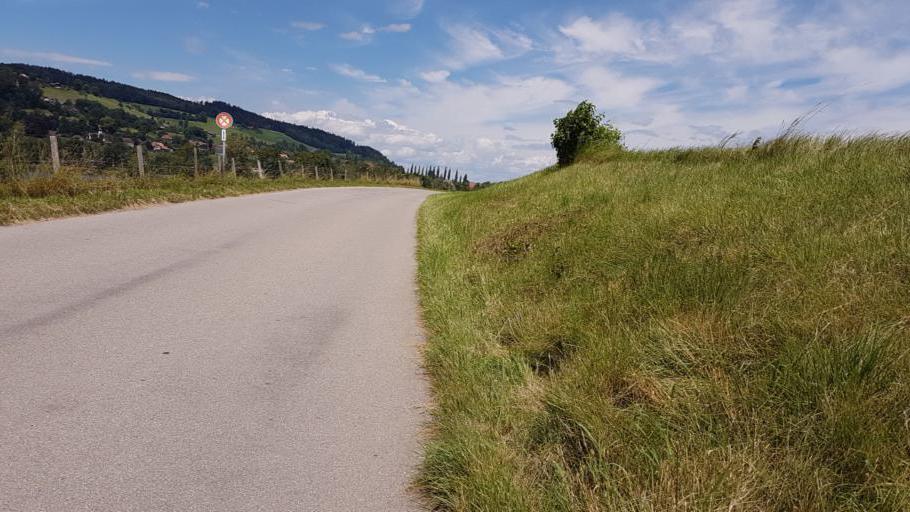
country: CH
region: Bern
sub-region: Bern-Mittelland District
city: Niederwichtrach
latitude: 46.8265
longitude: 7.5498
